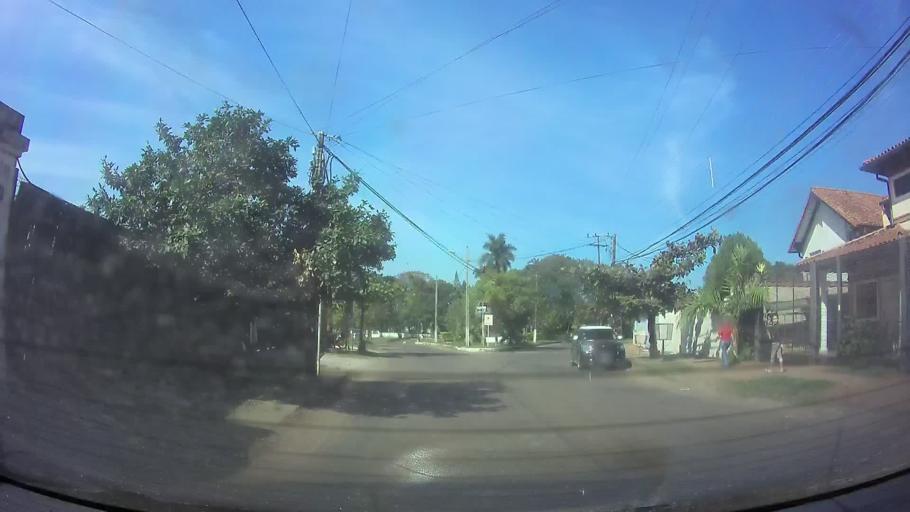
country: PY
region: Central
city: Fernando de la Mora
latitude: -25.2807
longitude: -57.5449
